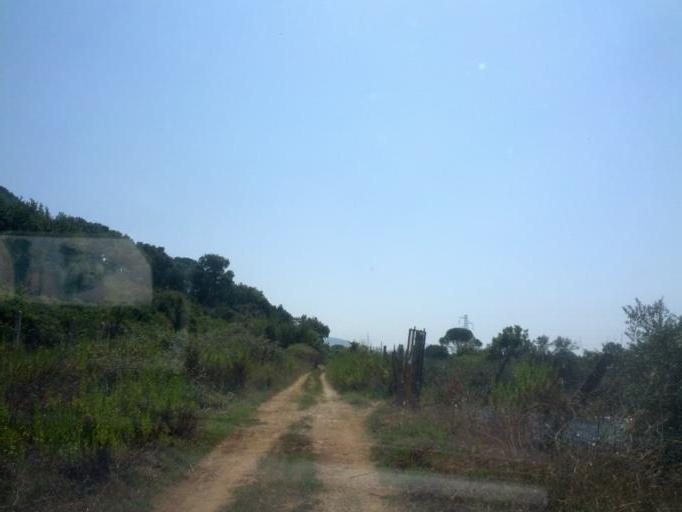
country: IT
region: Latium
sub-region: Provincia di Latina
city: Monte San Biagio
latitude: 41.3650
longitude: 13.3566
